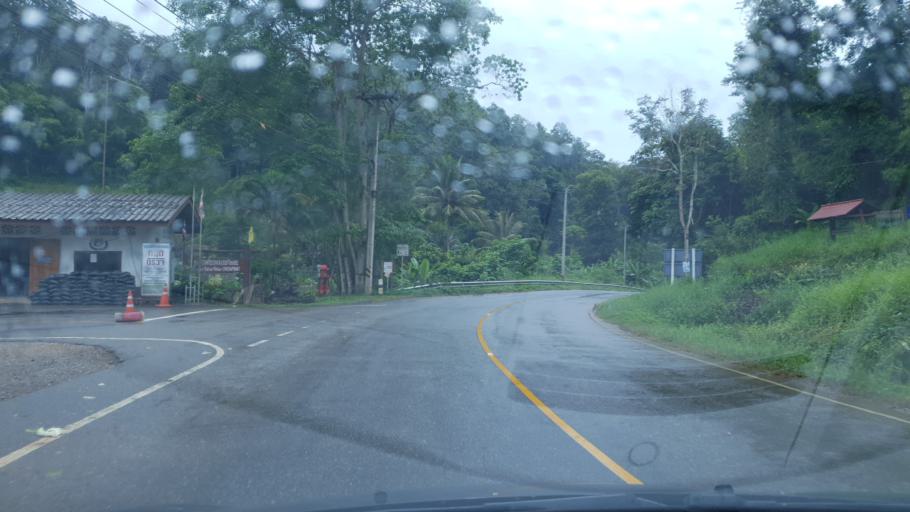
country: TH
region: Mae Hong Son
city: Mae La Noi
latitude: 18.5980
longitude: 97.9424
